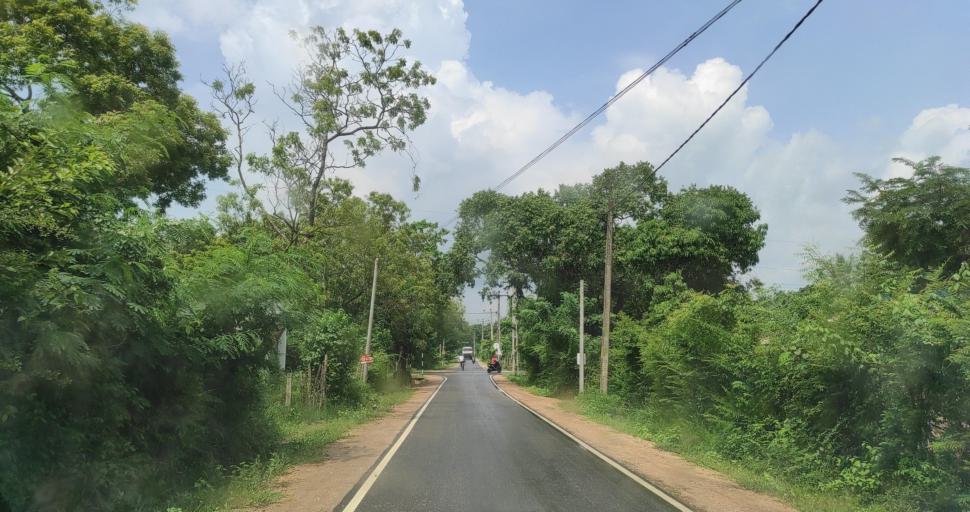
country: LK
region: Eastern Province
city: Trincomalee
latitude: 8.3719
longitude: 81.0121
